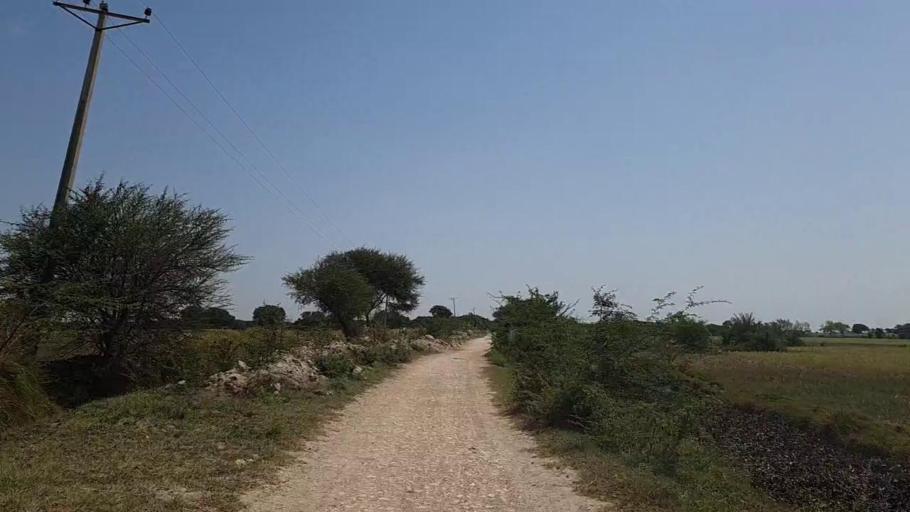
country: PK
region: Sindh
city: Mirpur Batoro
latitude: 24.7752
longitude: 68.2443
